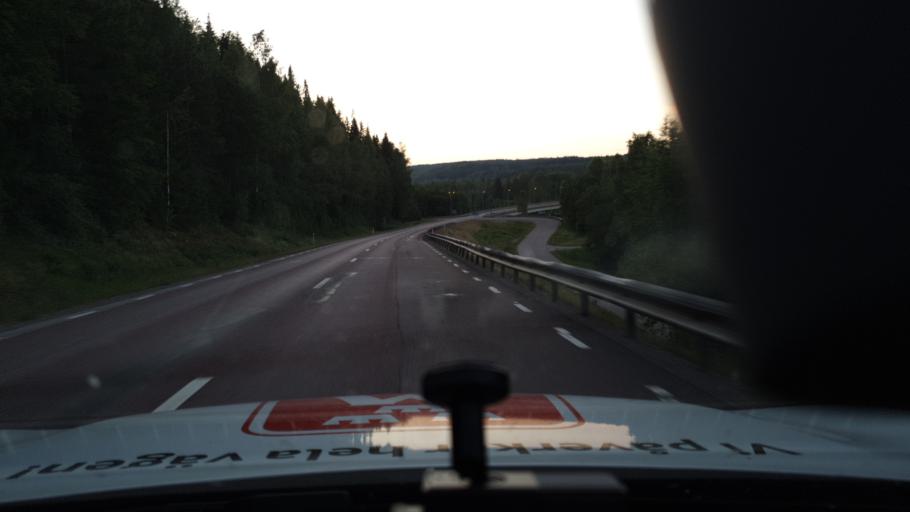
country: SE
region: Vaermland
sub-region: Hagfors Kommun
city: Ekshaerad
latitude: 60.4155
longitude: 13.2536
